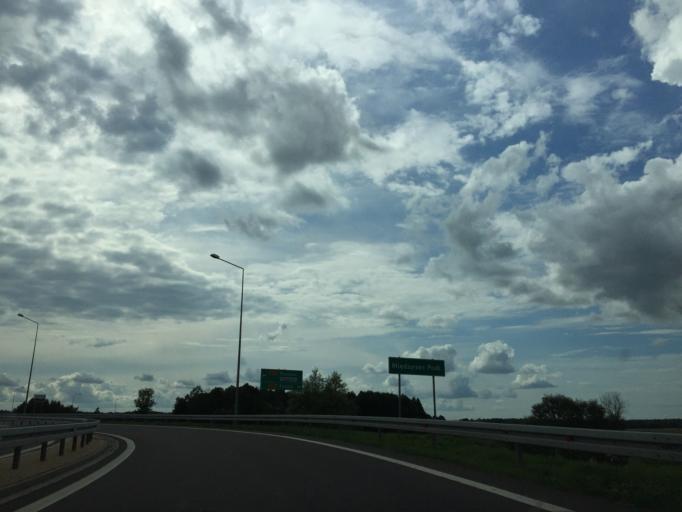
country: PL
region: Lublin Voivodeship
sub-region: Powiat bialski
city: Rzeczyca
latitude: 51.9762
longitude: 22.7428
